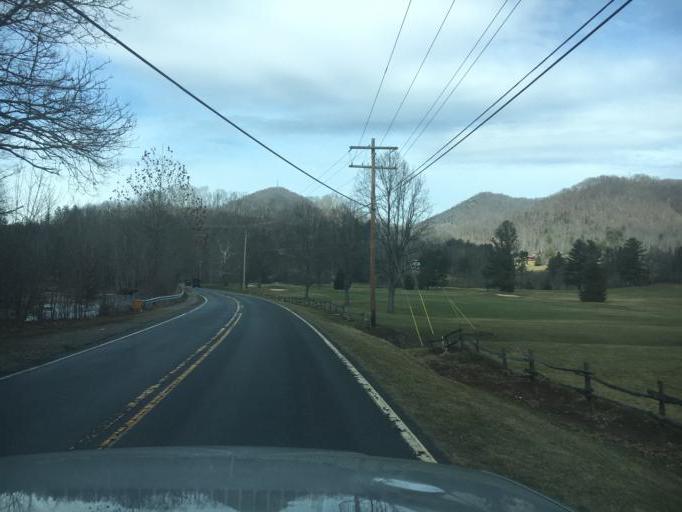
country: US
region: North Carolina
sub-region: Haywood County
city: Canton
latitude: 35.4419
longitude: -82.8137
